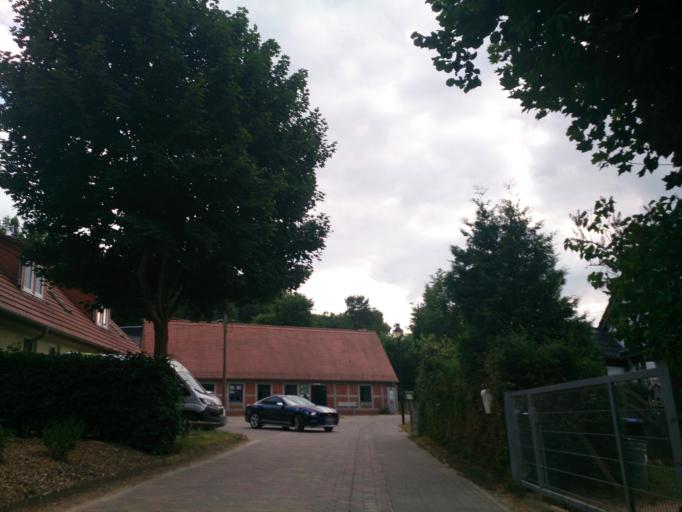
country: DE
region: Mecklenburg-Vorpommern
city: Plau am See
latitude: 53.4314
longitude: 12.3147
